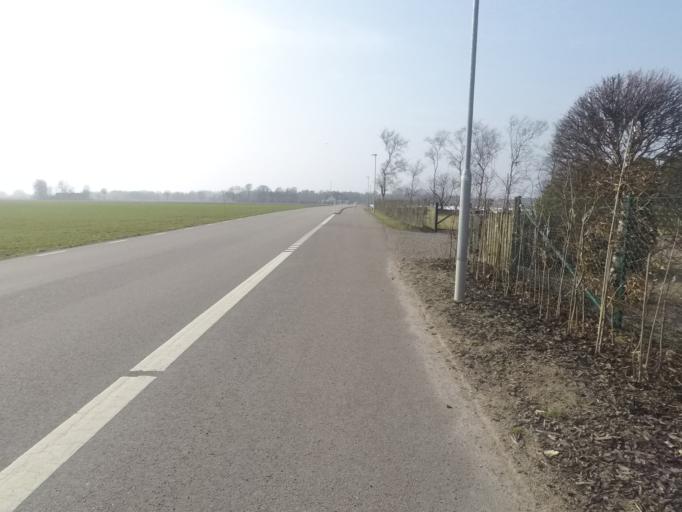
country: SE
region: Skane
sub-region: Helsingborg
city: Odakra
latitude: 56.2166
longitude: 12.6864
